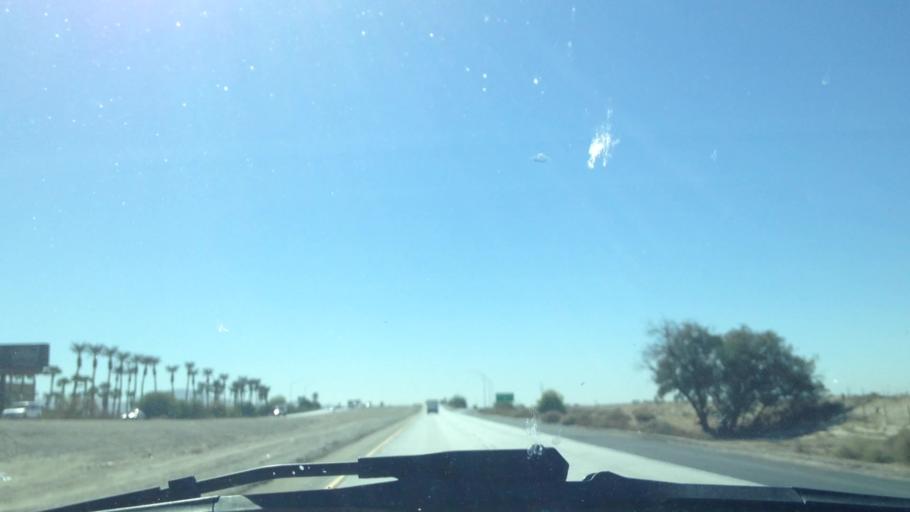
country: US
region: California
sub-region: Riverside County
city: Indio
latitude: 33.7128
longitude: -116.1876
